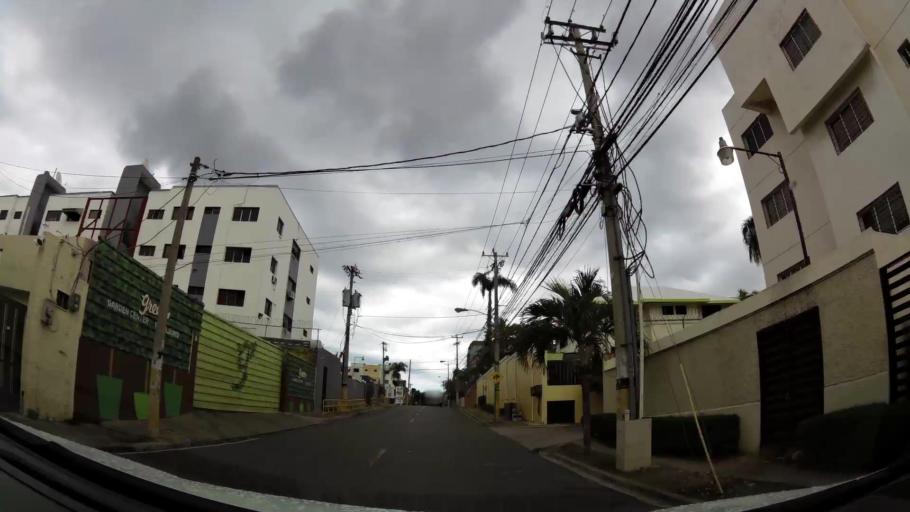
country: DO
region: Nacional
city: La Agustina
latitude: 18.4895
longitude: -69.9349
